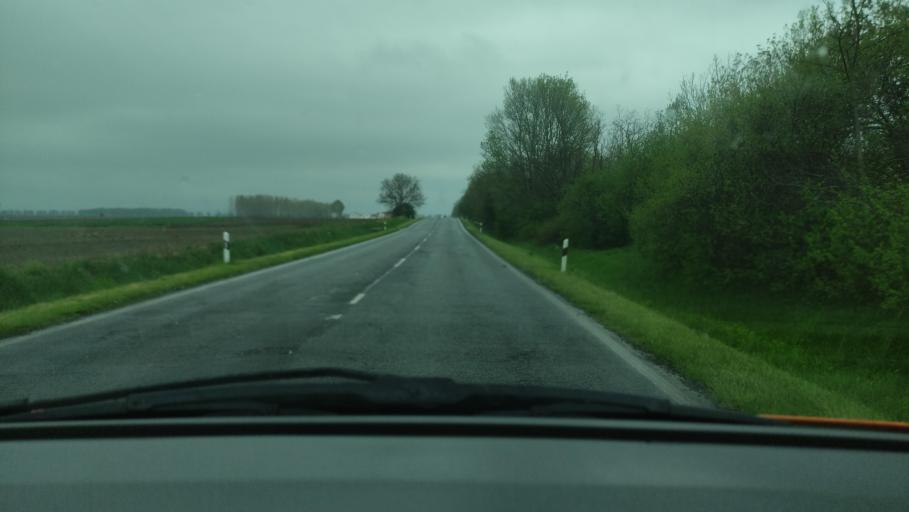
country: HU
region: Baranya
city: Mohacs
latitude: 45.9219
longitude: 18.6595
